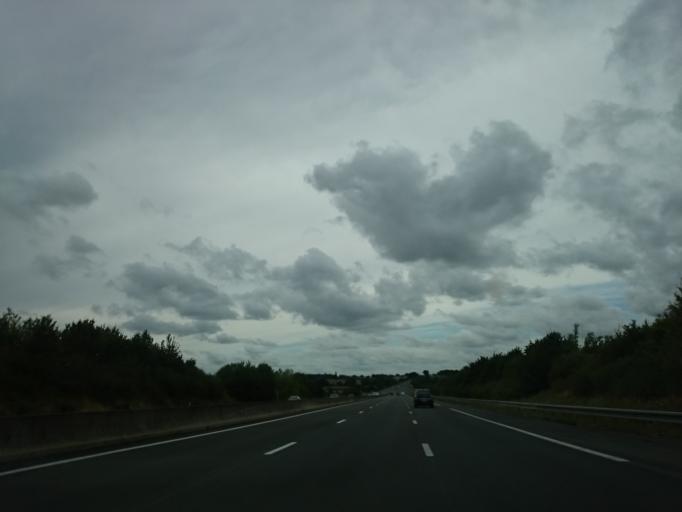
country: FR
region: Pays de la Loire
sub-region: Departement de la Sarthe
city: Cherre
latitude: 48.1624
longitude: 0.7252
